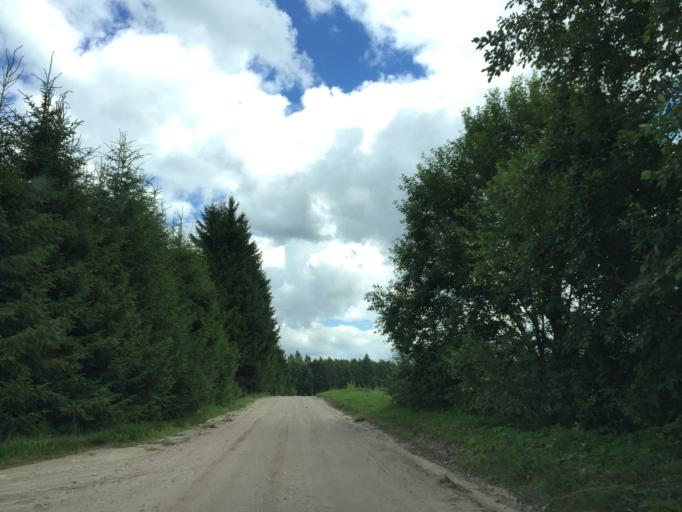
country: LV
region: Malpils
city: Malpils
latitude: 56.8943
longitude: 24.9667
